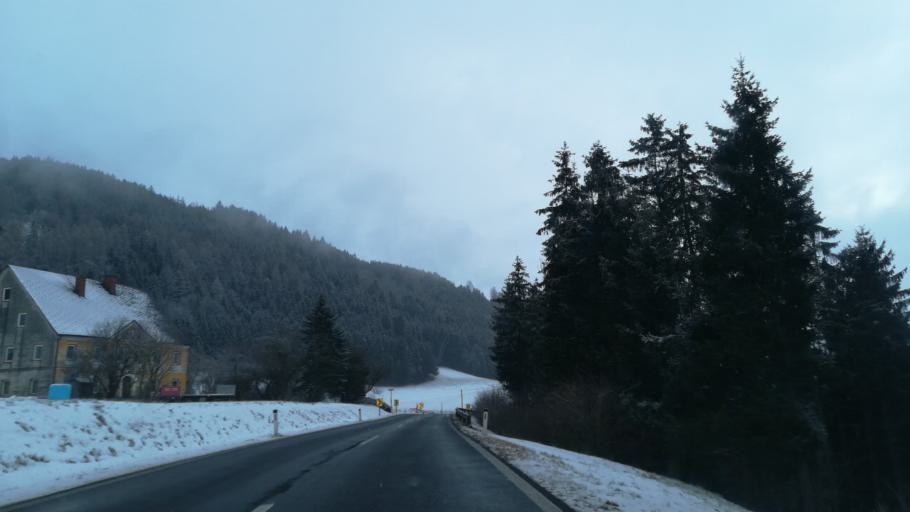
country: AT
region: Styria
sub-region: Politischer Bezirk Murtal
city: Poels
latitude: 47.2178
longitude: 14.6125
